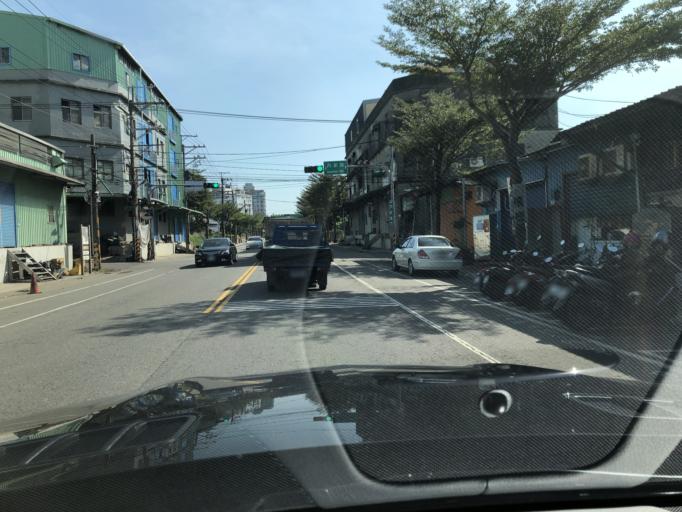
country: TW
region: Taiwan
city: Taoyuan City
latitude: 25.0709
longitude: 121.2886
